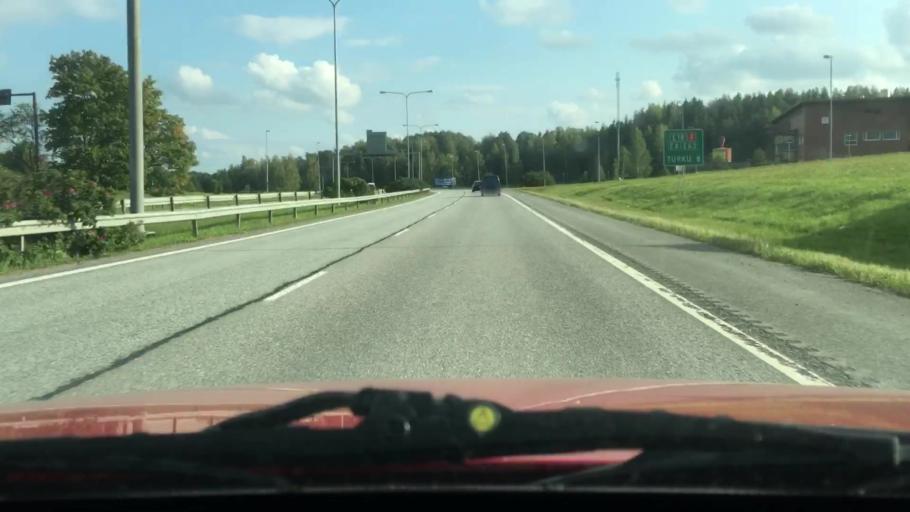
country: FI
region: Varsinais-Suomi
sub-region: Turku
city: Raisio
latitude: 60.4818
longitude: 22.1812
